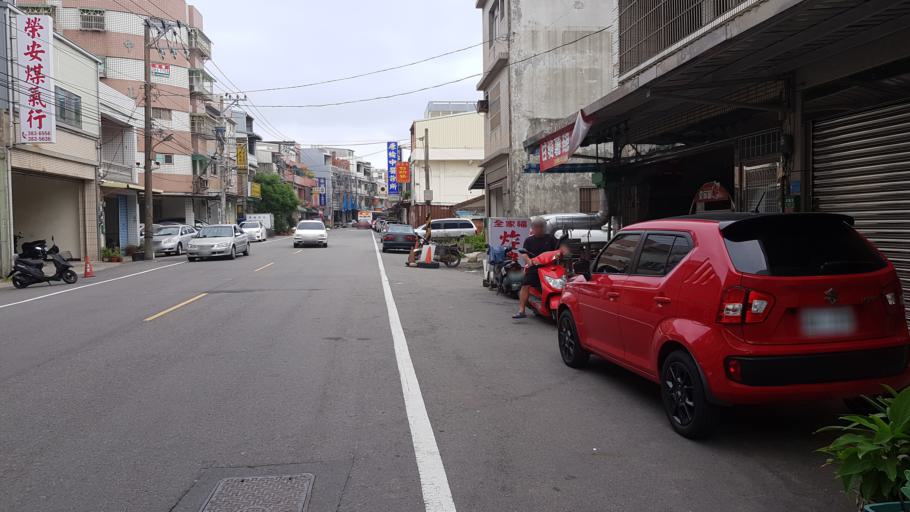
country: TW
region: Taiwan
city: Taoyuan City
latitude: 25.0793
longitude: 121.2569
